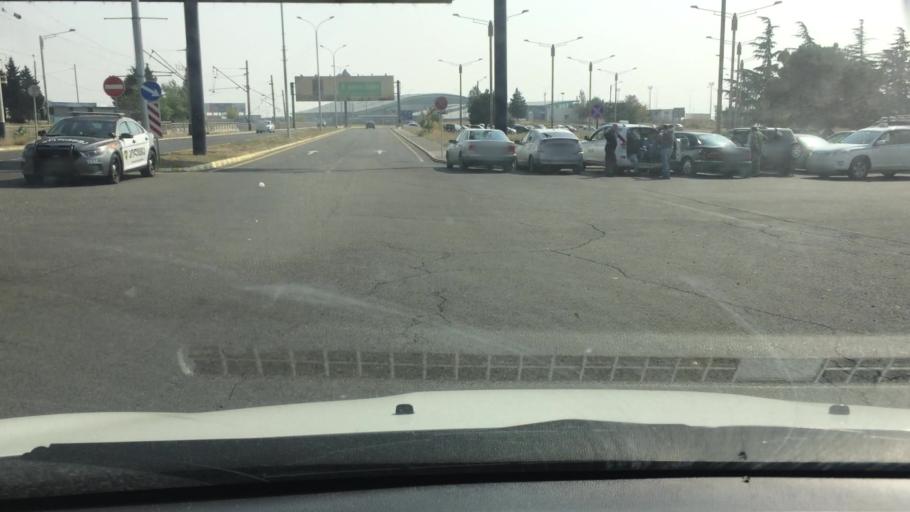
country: GE
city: Didi Lilo
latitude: 41.6743
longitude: 44.9617
